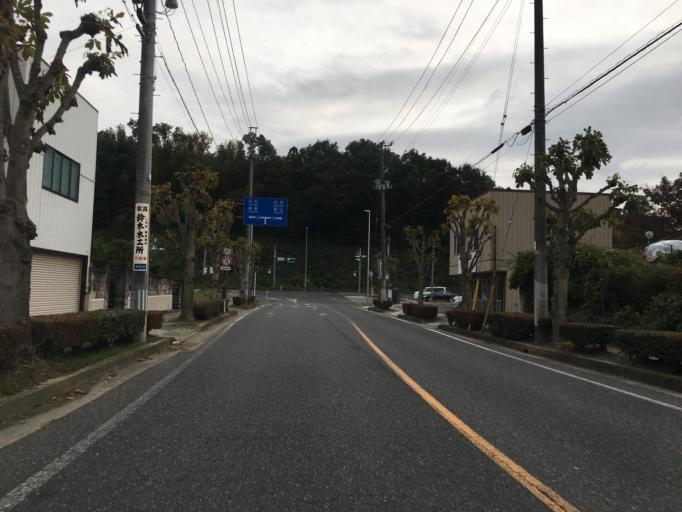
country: JP
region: Fukushima
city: Nihommatsu
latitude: 37.5833
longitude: 140.4333
